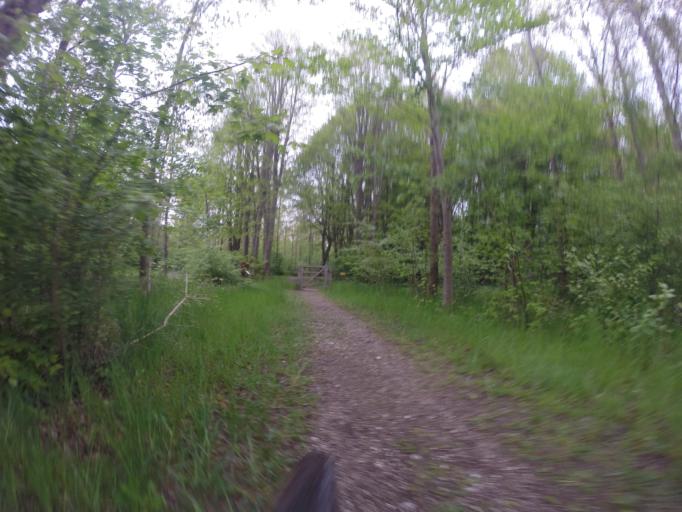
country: DK
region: Capital Region
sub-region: Ballerup Kommune
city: Ballerup
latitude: 55.6954
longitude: 12.3476
